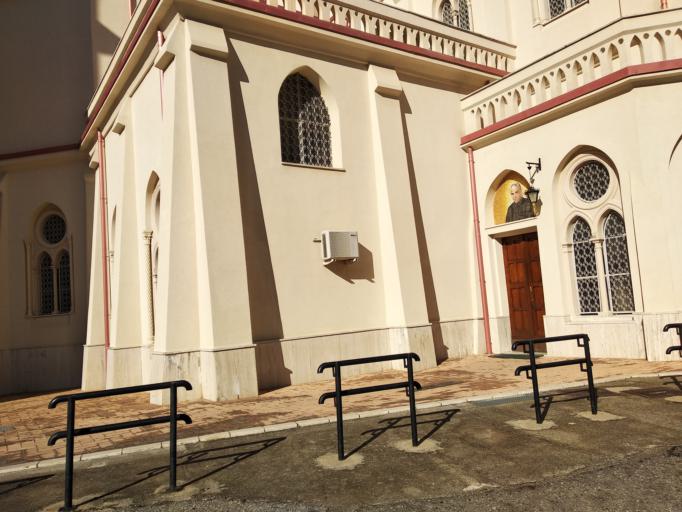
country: IT
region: Calabria
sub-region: Provincia di Reggio Calabria
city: Reggio Calabria
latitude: 38.1105
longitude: 15.6568
